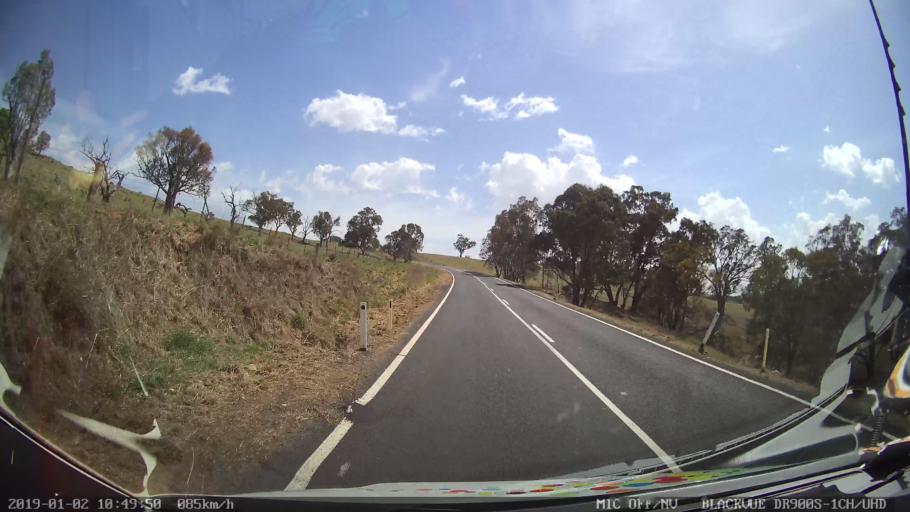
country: AU
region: New South Wales
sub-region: Cootamundra
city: Cootamundra
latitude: -34.7196
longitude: 148.2767
